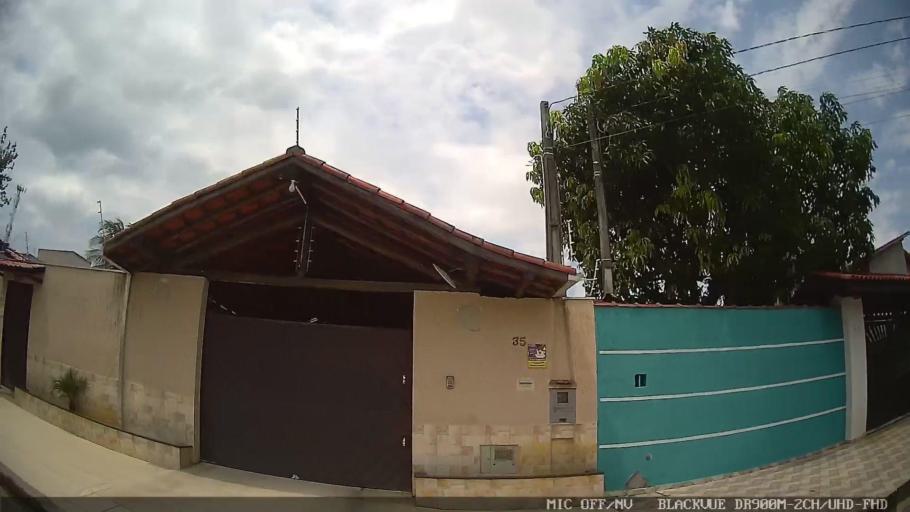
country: BR
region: Sao Paulo
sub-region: Caraguatatuba
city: Caraguatatuba
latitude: -23.6667
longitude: -45.4378
